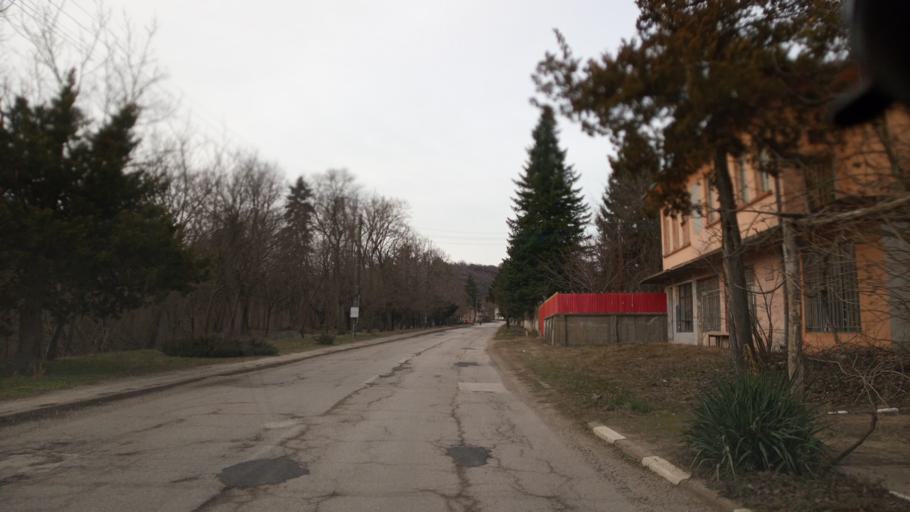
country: BG
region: Pleven
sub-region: Obshtina Belene
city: Belene
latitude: 43.6051
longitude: 25.0016
